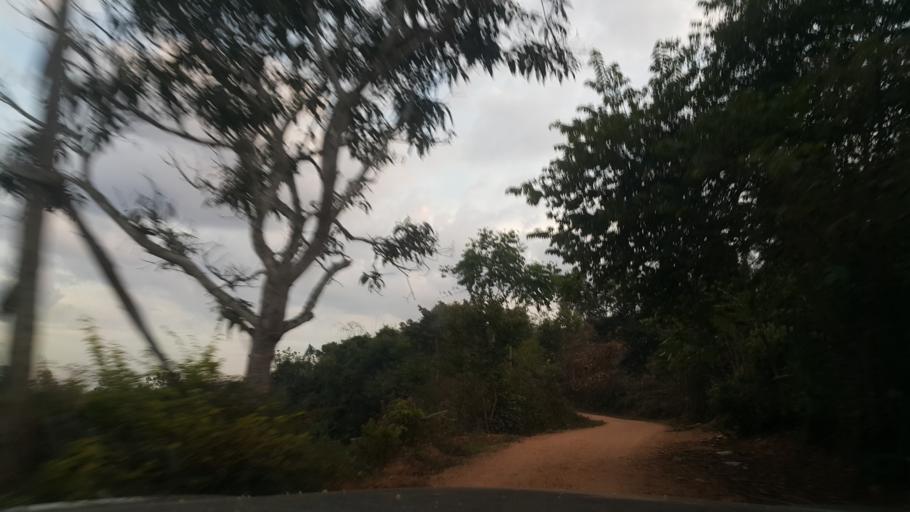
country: TH
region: Chiang Mai
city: Samoeng
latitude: 18.9594
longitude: 98.6727
